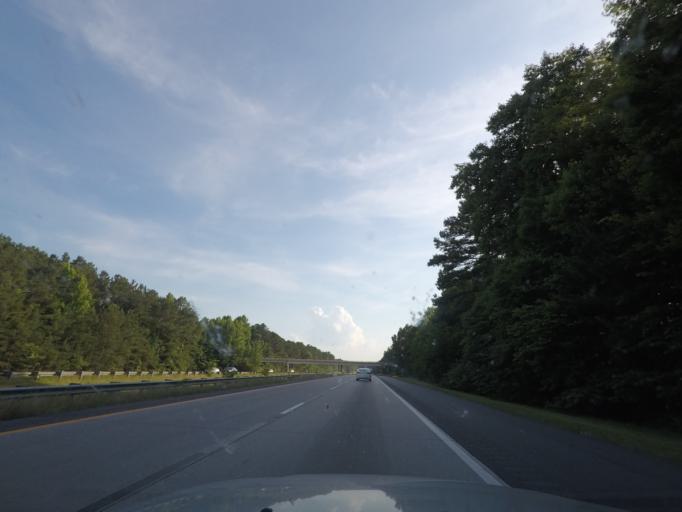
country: US
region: North Carolina
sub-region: Granville County
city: Creedmoor
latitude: 36.2203
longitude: -78.6614
